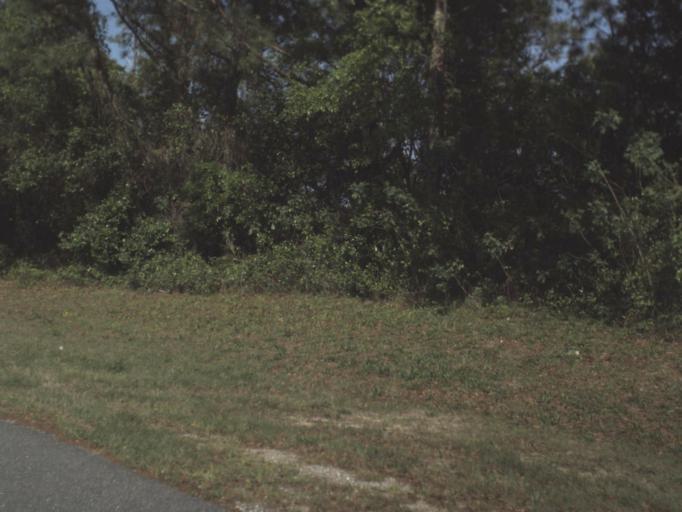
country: US
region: Florida
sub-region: Escambia County
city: East Pensacola Heights
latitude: 30.4559
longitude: -87.1688
